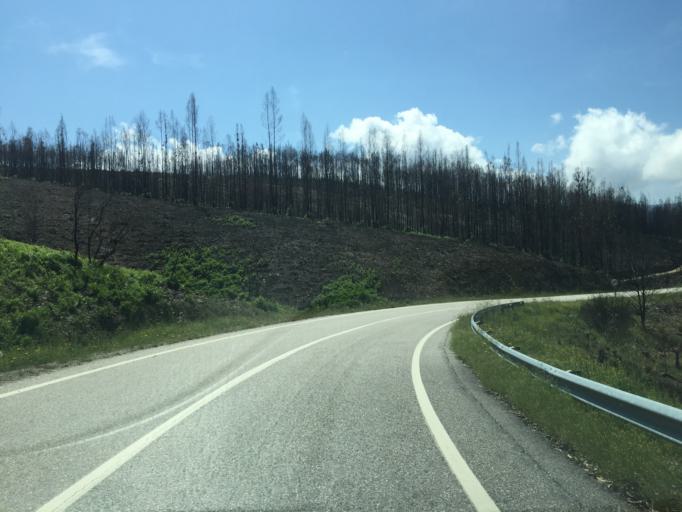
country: PT
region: Coimbra
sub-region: Pampilhosa da Serra
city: Pampilhosa da Serra
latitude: 39.9979
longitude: -7.9727
